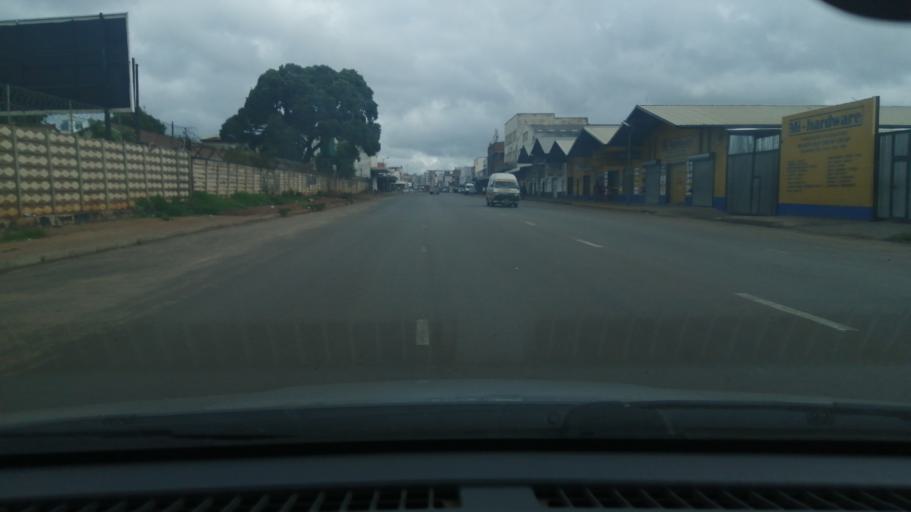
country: ZW
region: Harare
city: Harare
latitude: -17.8410
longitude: 31.0431
